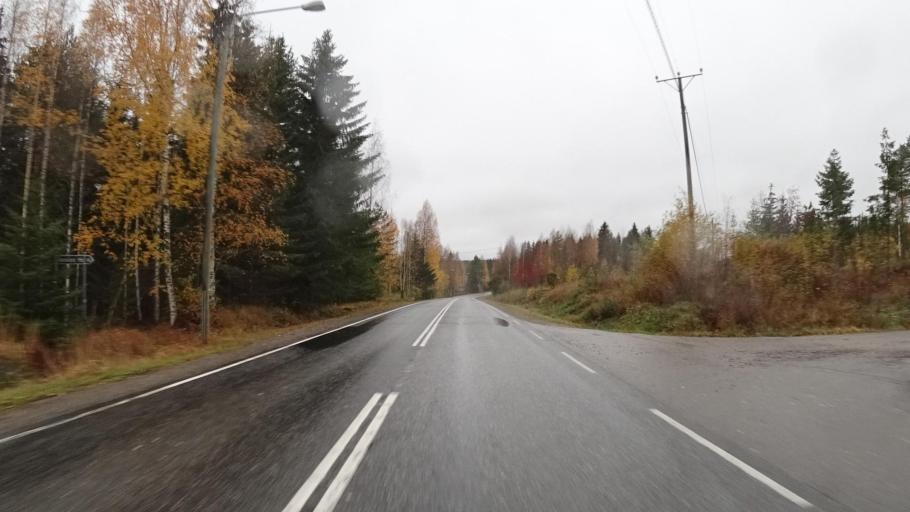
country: FI
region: Northern Savo
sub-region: Koillis-Savo
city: Tuusniemi
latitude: 62.7929
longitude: 28.5543
